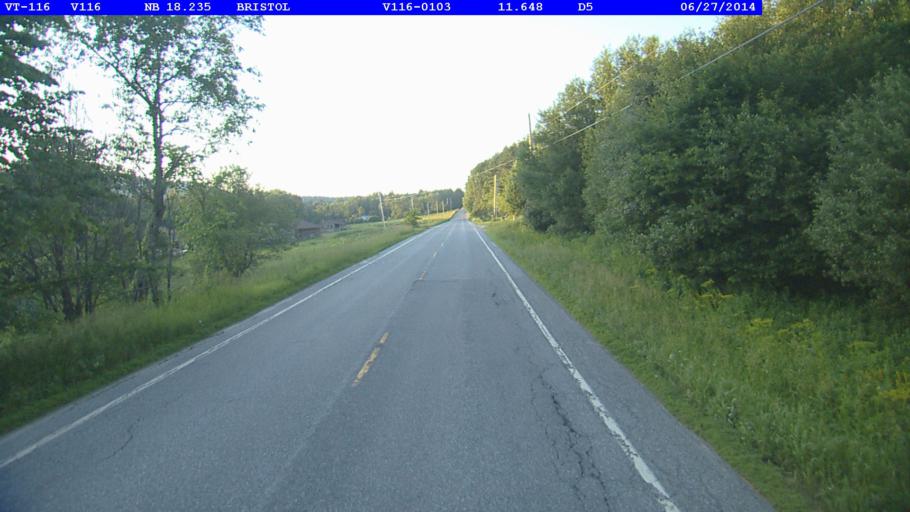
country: US
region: Vermont
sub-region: Addison County
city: Bristol
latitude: 44.1768
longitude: -73.0571
